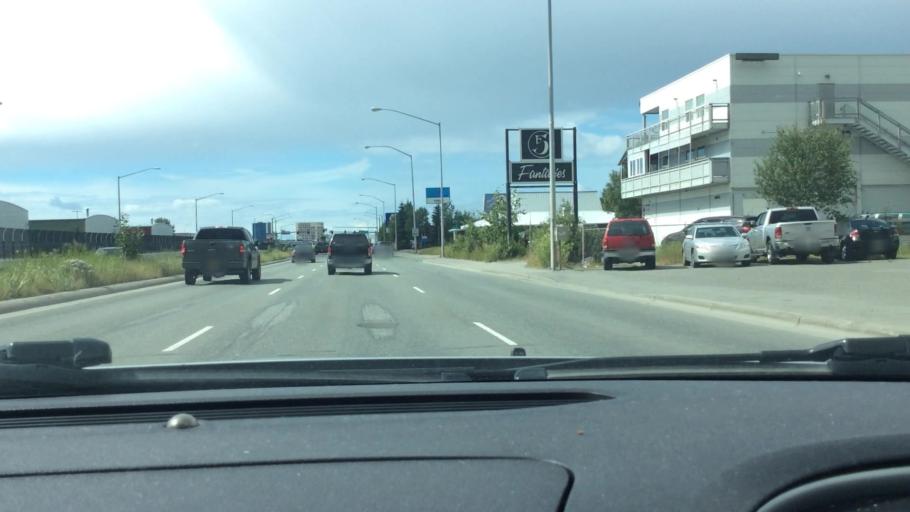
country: US
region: Alaska
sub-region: Anchorage Municipality
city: Anchorage
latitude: 61.2176
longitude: -149.8440
